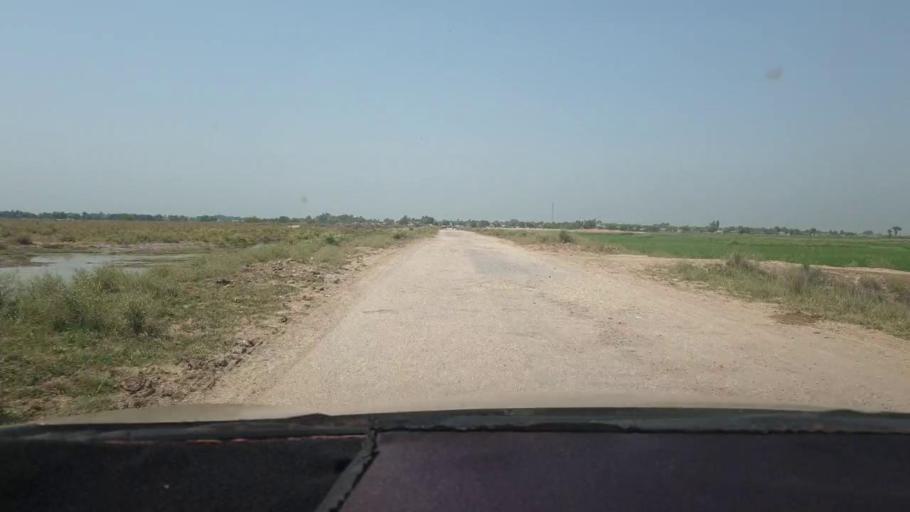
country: PK
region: Sindh
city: Miro Khan
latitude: 27.6644
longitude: 68.0710
